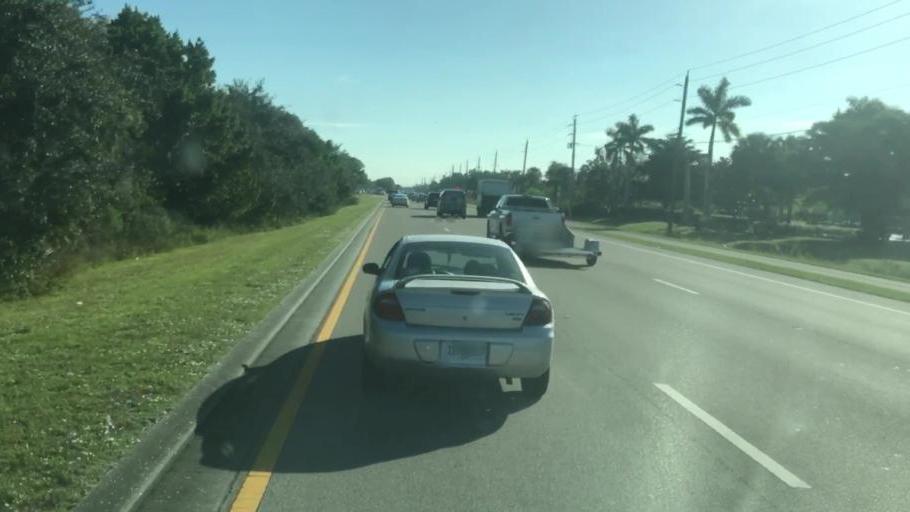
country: US
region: Florida
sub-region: Lee County
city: Villas
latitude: 26.5471
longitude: -81.8115
